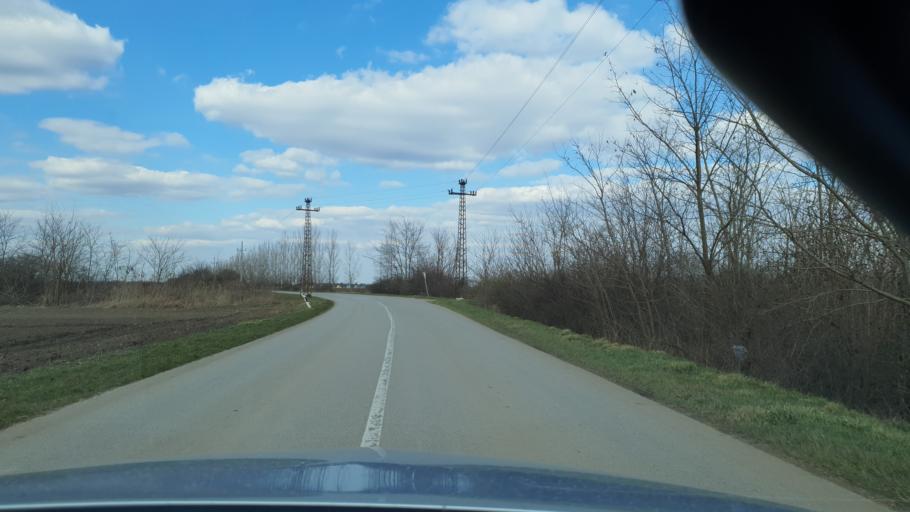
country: RS
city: Ravno Selo
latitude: 45.4317
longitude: 19.6054
